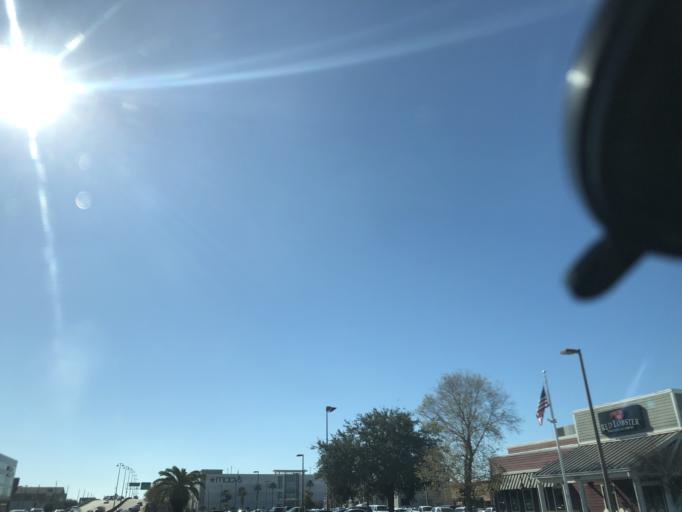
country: US
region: Louisiana
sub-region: Jefferson Parish
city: Metairie
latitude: 30.0079
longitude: -90.1553
